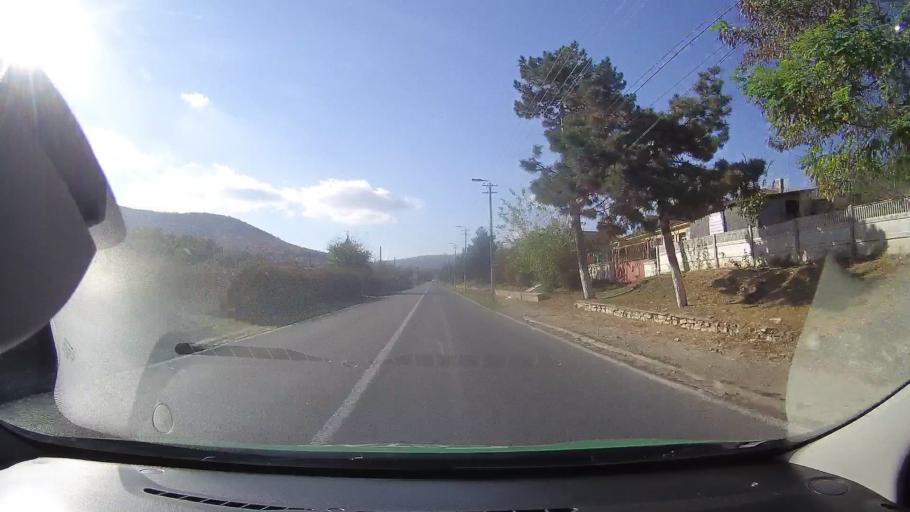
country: RO
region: Tulcea
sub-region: Oras Babadag
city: Babadag
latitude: 44.8881
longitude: 28.7062
